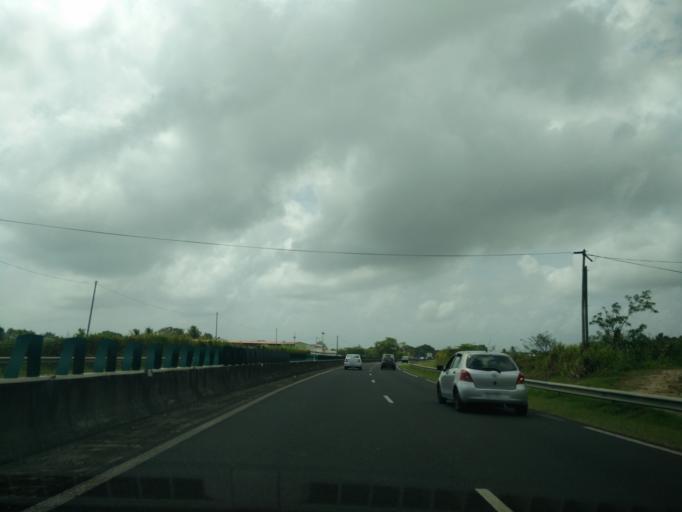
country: GP
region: Guadeloupe
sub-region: Guadeloupe
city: Petit-Bourg
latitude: 16.1807
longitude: -61.5990
